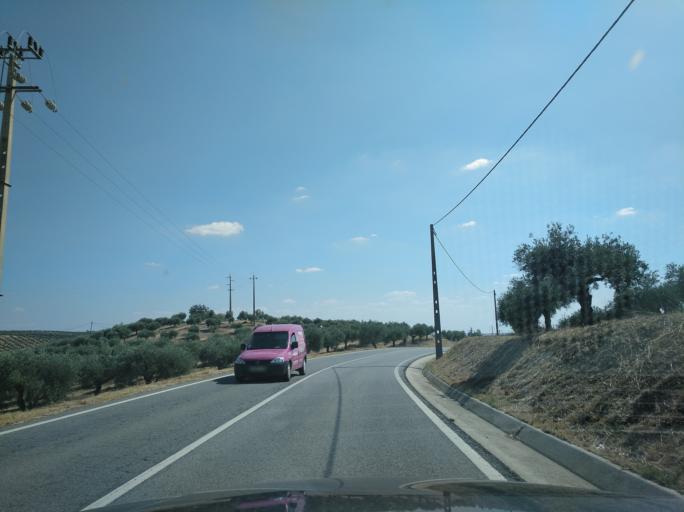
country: PT
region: Portalegre
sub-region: Campo Maior
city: Campo Maior
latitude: 39.0005
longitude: -7.0714
